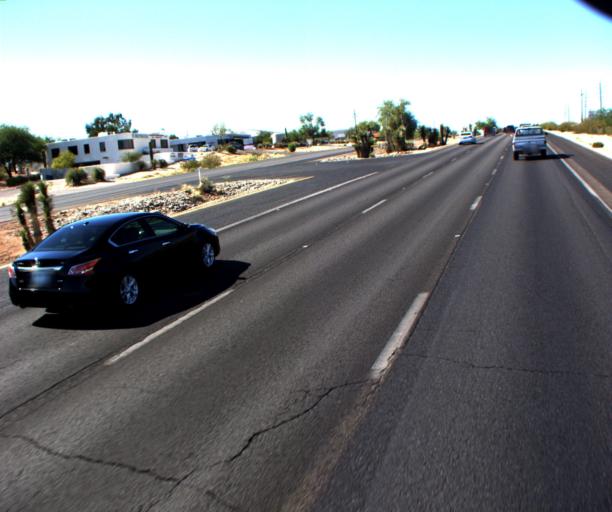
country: US
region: Arizona
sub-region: Pima County
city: Casas Adobes
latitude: 32.3065
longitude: -110.9784
